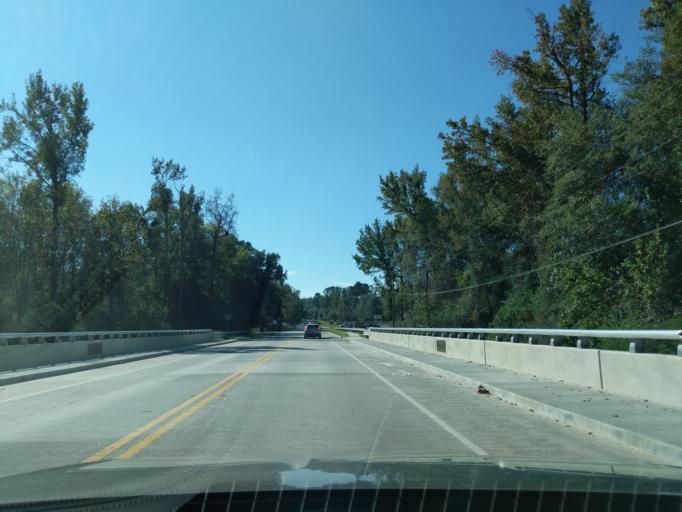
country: US
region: Georgia
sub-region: Richmond County
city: Hephzibah
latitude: 33.3449
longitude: -82.0049
